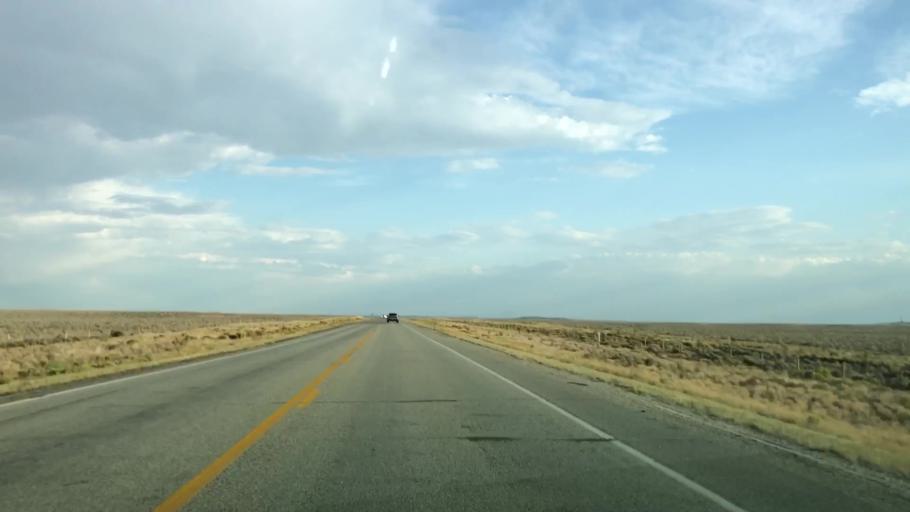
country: US
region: Wyoming
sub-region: Sublette County
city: Pinedale
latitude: 42.4119
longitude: -109.5531
